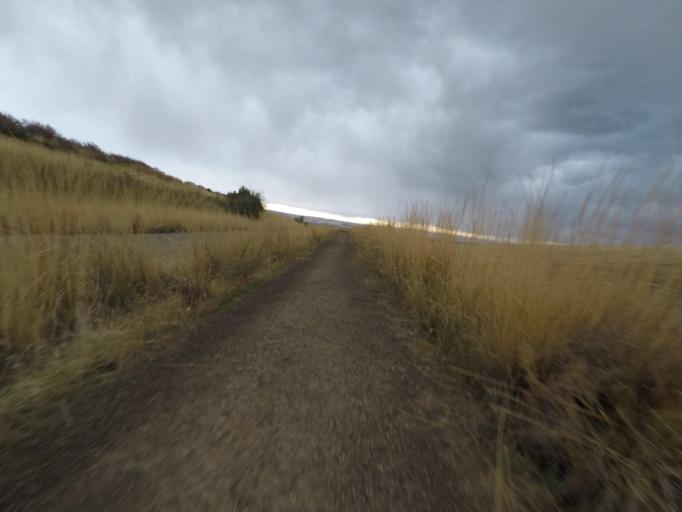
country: US
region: Washington
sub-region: Walla Walla County
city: Walla Walla East
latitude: 46.0661
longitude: -118.2684
